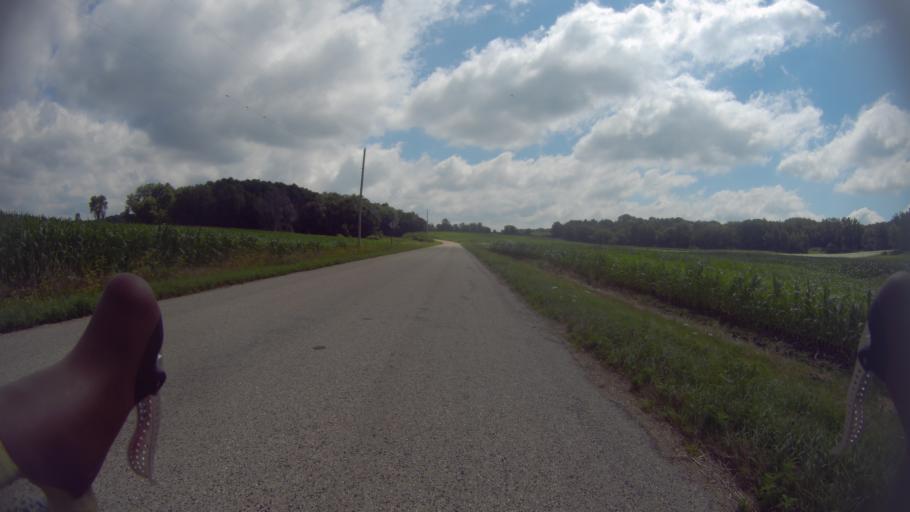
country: US
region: Wisconsin
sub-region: Columbia County
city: Lodi
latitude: 43.2276
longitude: -89.6073
